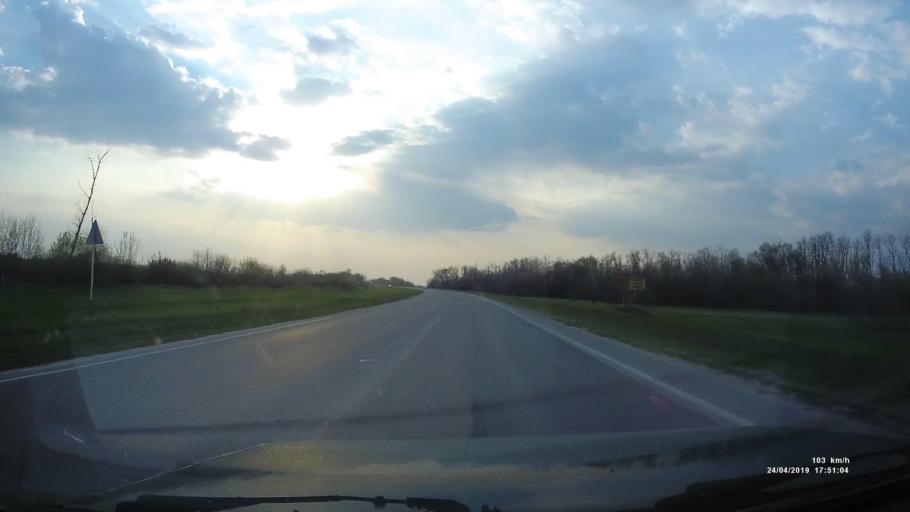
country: RU
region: Rostov
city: Yegorlykskaya
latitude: 46.5443
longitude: 40.7675
